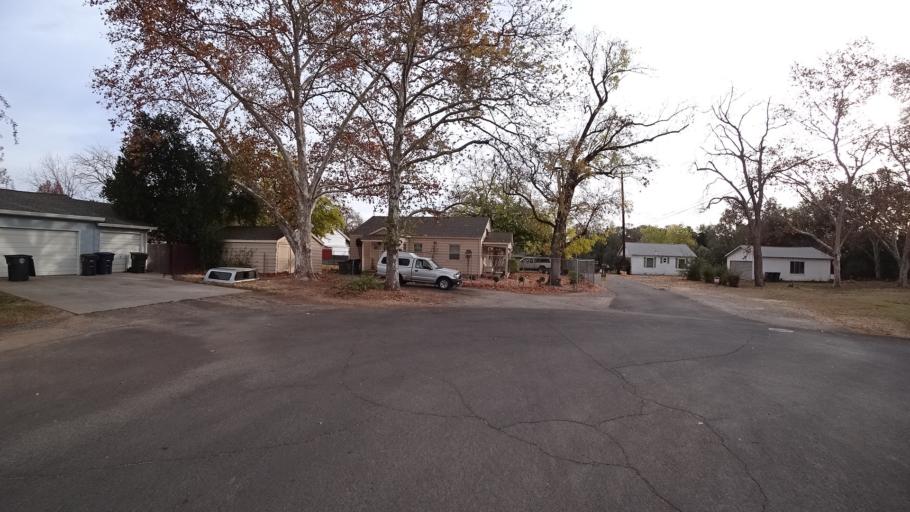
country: US
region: California
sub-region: Sacramento County
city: Citrus Heights
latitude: 38.7134
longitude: -121.2833
